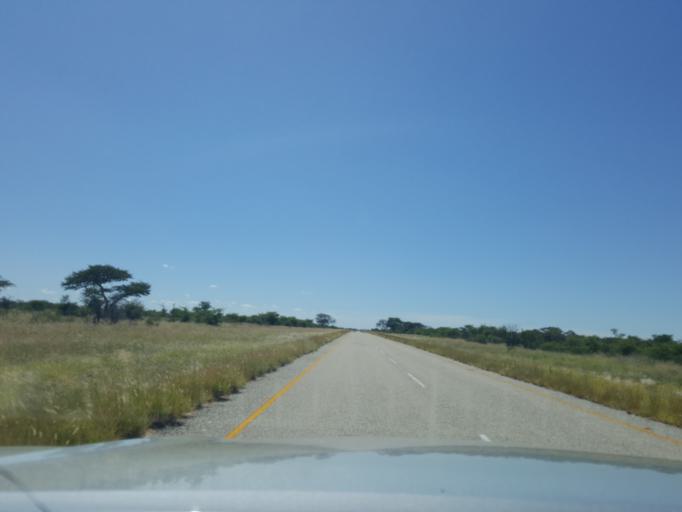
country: BW
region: Central
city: Gweta
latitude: -20.2258
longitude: 25.0024
